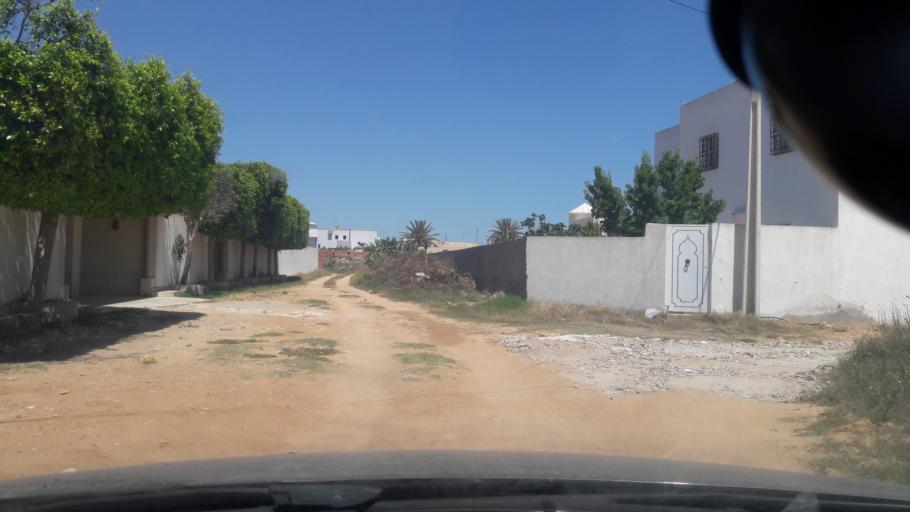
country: TN
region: Safaqis
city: Al Qarmadah
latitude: 34.8109
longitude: 10.7565
